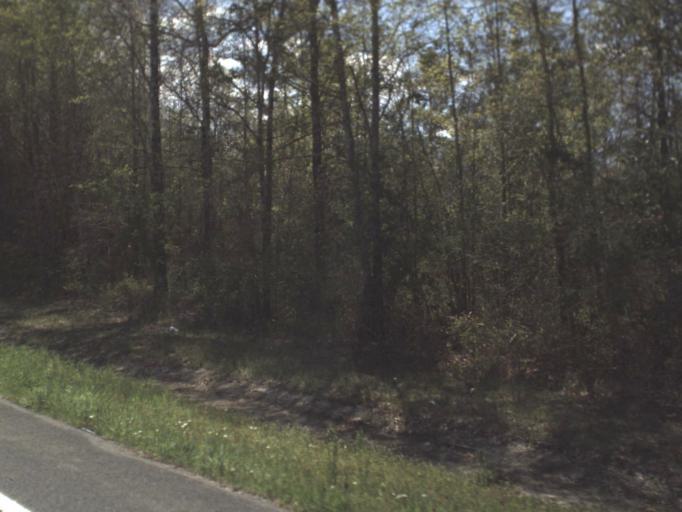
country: US
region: Alabama
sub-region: Geneva County
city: Geneva
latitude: 30.9285
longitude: -85.9650
